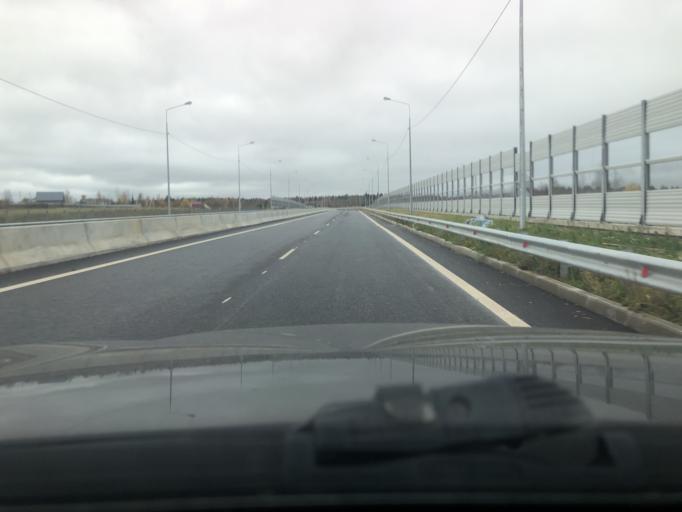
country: RU
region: Moskovskaya
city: Semkhoz
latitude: 56.3276
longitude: 38.0775
